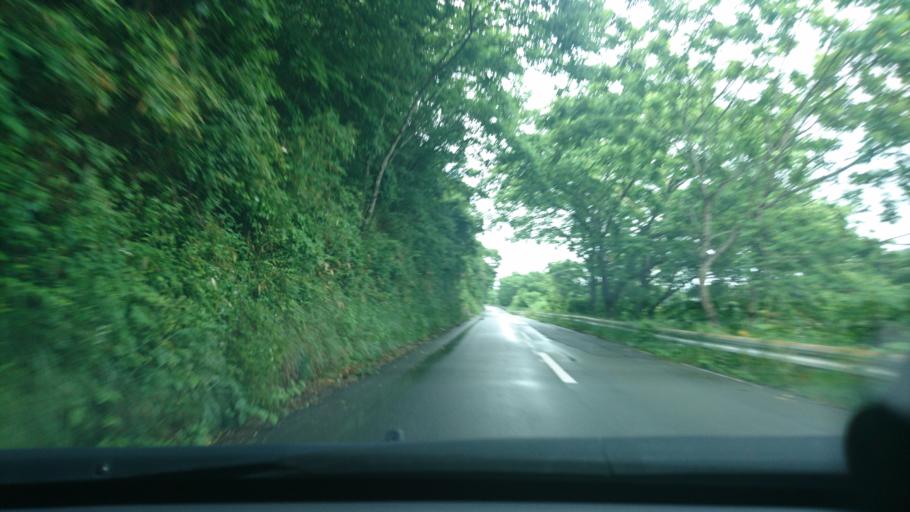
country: JP
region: Miyagi
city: Wakuya
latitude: 38.6763
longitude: 141.2836
